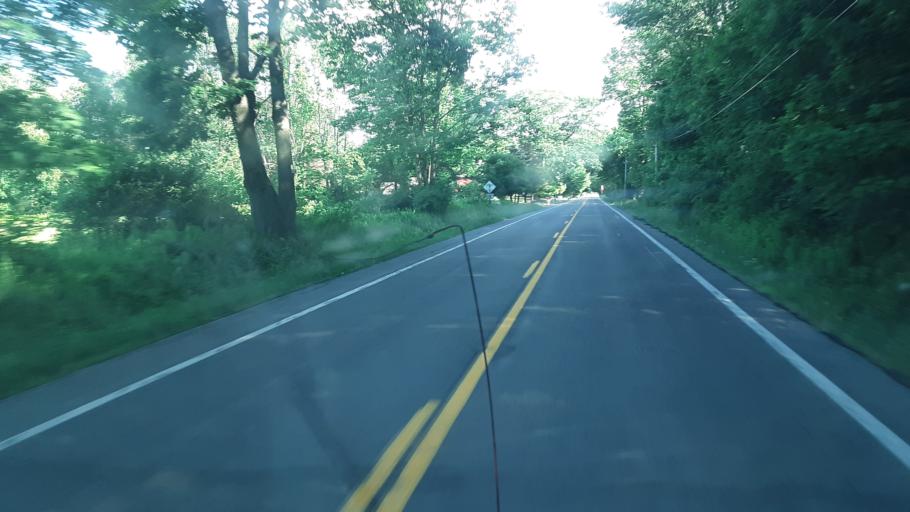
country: US
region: New York
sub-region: Oneida County
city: Rome
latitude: 43.3200
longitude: -75.4762
